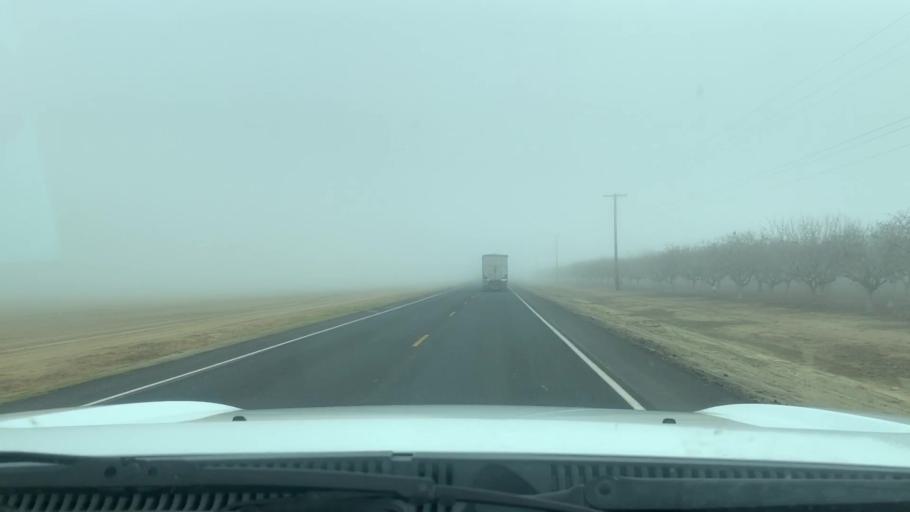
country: US
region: California
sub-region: Kern County
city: Lost Hills
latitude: 35.4994
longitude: -119.6252
